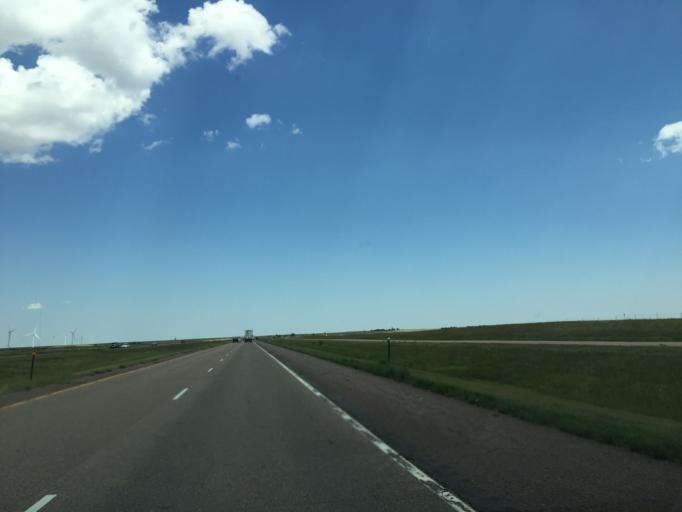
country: US
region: Colorado
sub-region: Lincoln County
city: Hugo
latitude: 39.2787
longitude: -103.4145
